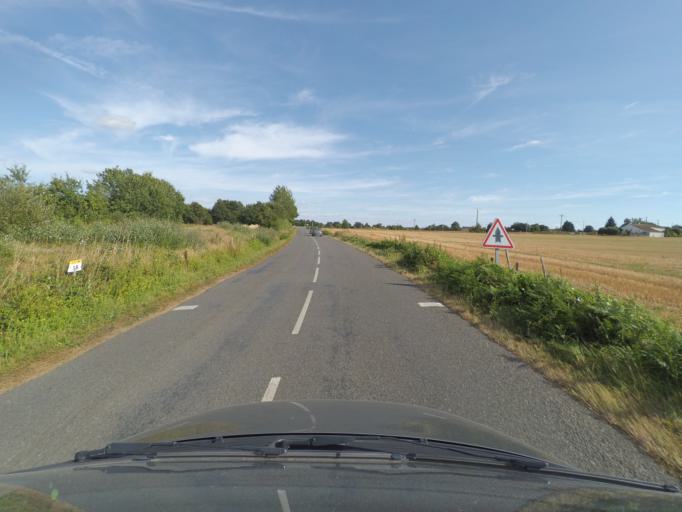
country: FR
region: Pays de la Loire
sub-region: Departement de la Loire-Atlantique
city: Montbert
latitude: 47.0290
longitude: -1.4685
